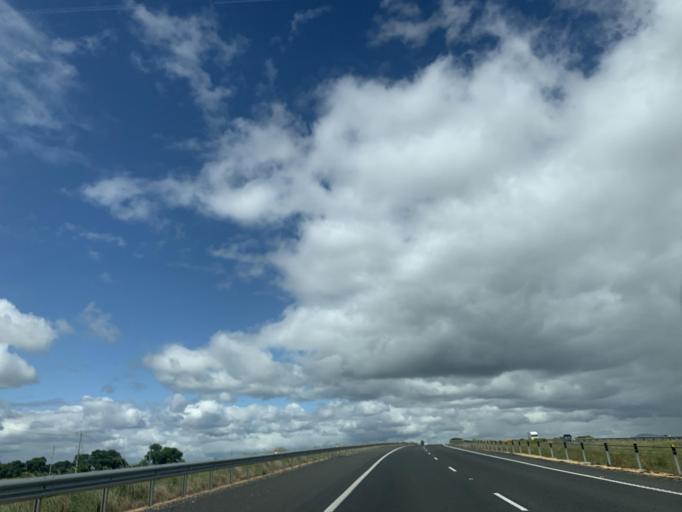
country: AU
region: Victoria
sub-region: Ballarat North
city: Newington
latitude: -37.4750
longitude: 143.6714
